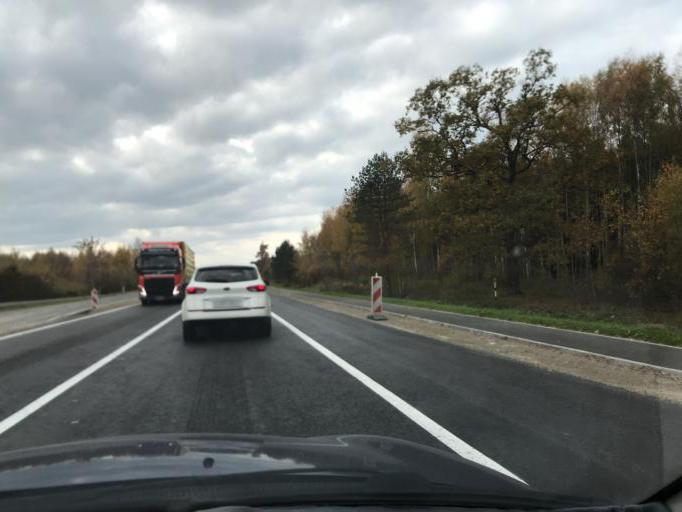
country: BY
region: Grodnenskaya
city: Lida
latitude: 53.8453
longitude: 25.1829
